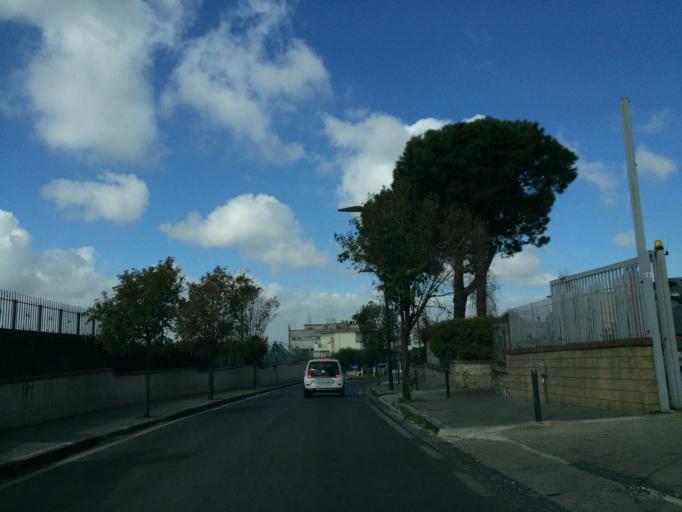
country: IT
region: Campania
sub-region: Provincia di Napoli
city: Pollena Trocchia
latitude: 40.8500
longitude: 14.3749
